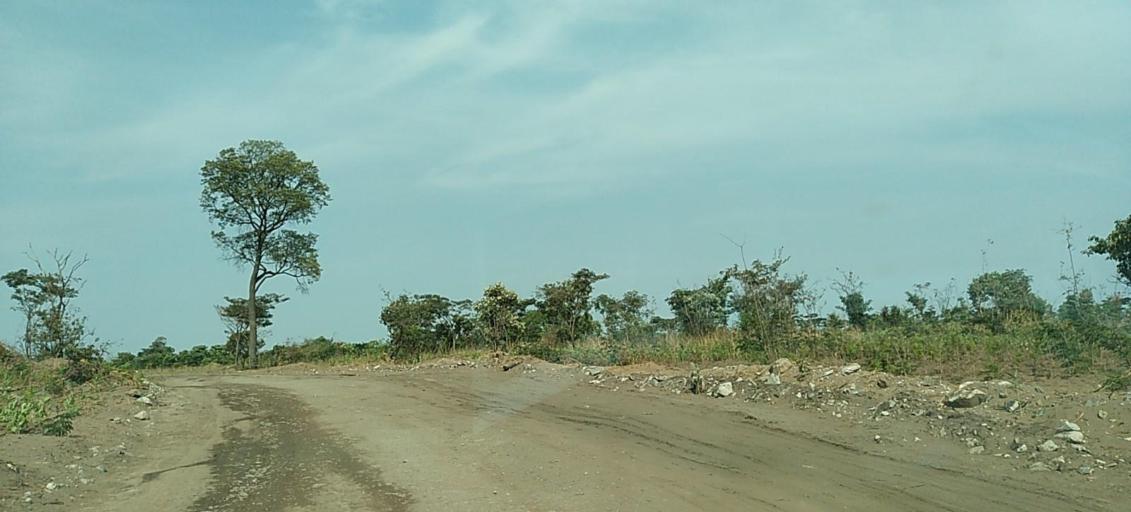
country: ZM
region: Copperbelt
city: Chililabombwe
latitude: -12.2918
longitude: 27.7639
